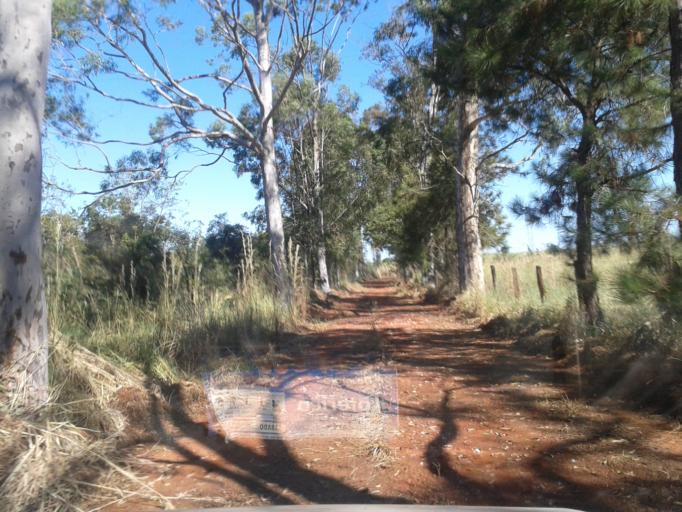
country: BR
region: Minas Gerais
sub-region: Santa Vitoria
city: Santa Vitoria
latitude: -19.0614
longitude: -50.3834
